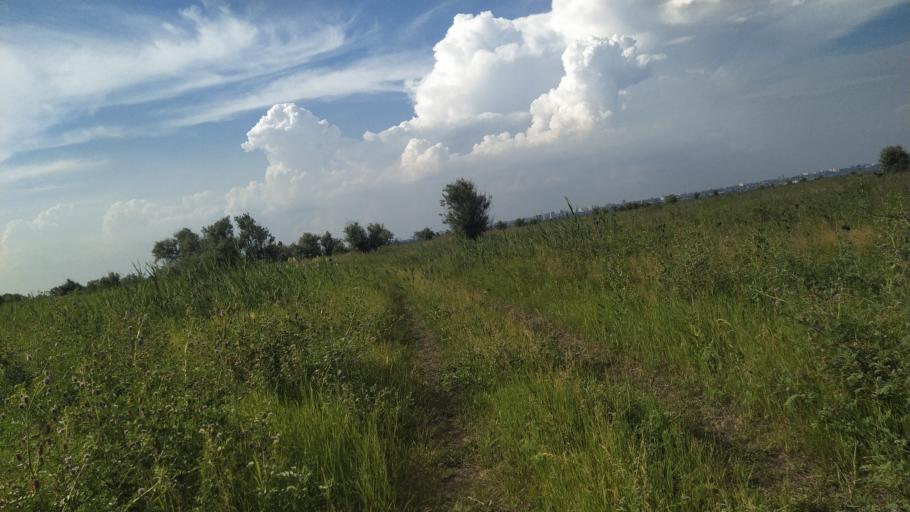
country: RU
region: Rostov
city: Kuleshovka
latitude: 47.1241
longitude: 39.6218
